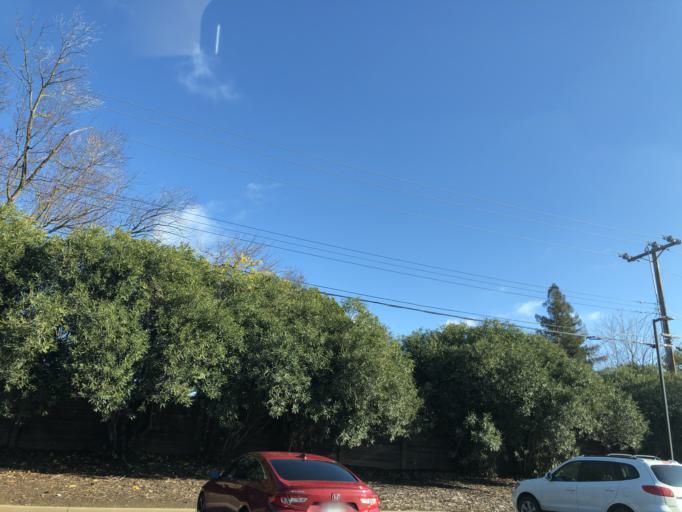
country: US
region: California
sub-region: Sacramento County
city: Rosemont
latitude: 38.5519
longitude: -121.4041
